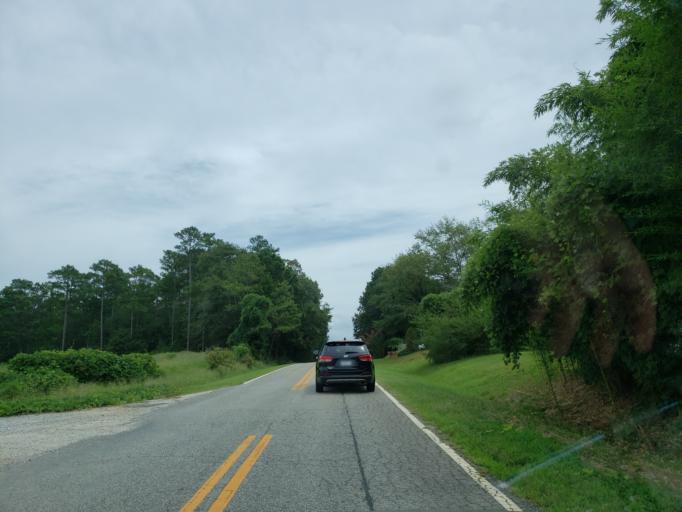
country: US
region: Georgia
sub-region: Lamar County
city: Barnesville
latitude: 33.1608
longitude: -84.0751
